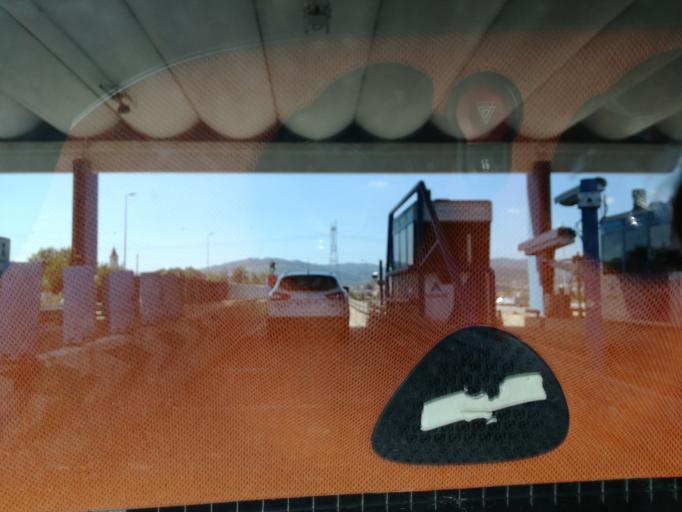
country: PT
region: Braga
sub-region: Guimaraes
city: Candoso
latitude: 41.4446
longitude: -8.3326
